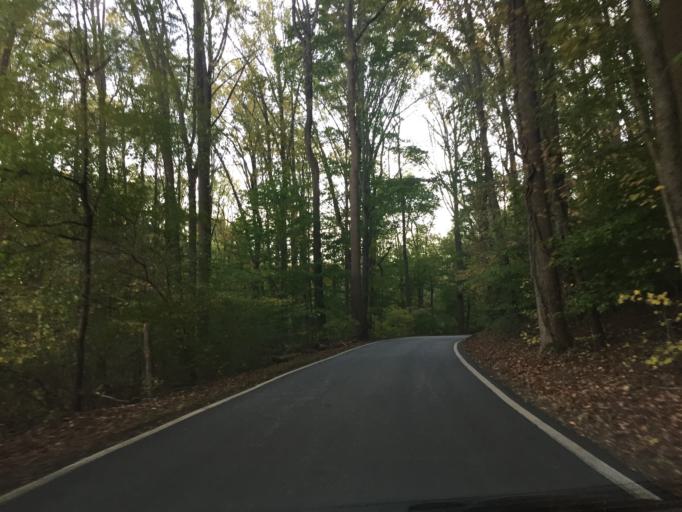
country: US
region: Maryland
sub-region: Baltimore County
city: Perry Hall
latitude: 39.4340
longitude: -76.4951
